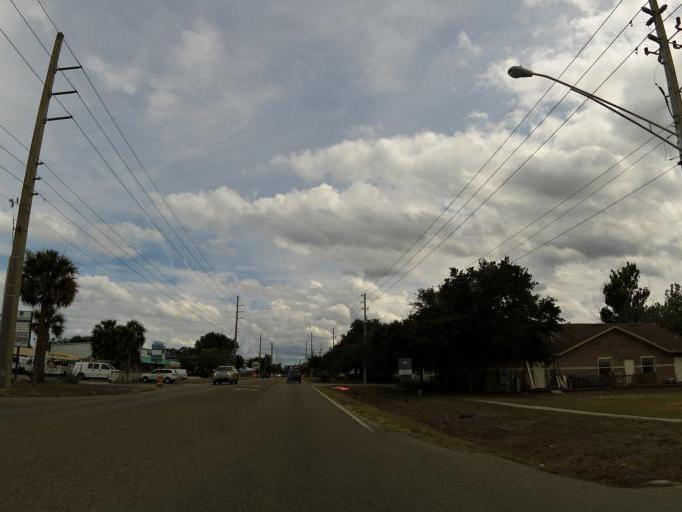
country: US
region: Florida
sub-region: Duval County
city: Neptune Beach
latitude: 30.3026
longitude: -81.4066
